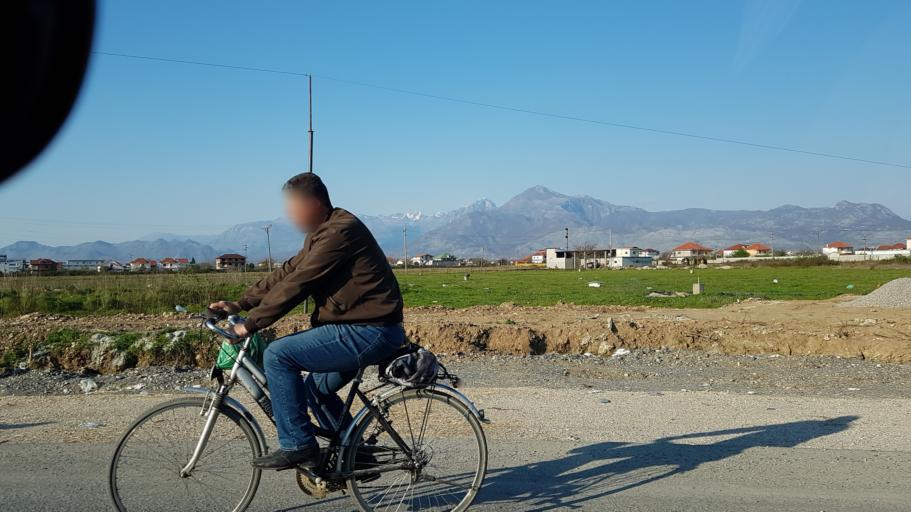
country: AL
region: Shkoder
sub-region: Rrethi i Shkodres
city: Shkoder
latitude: 42.0894
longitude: 19.5076
